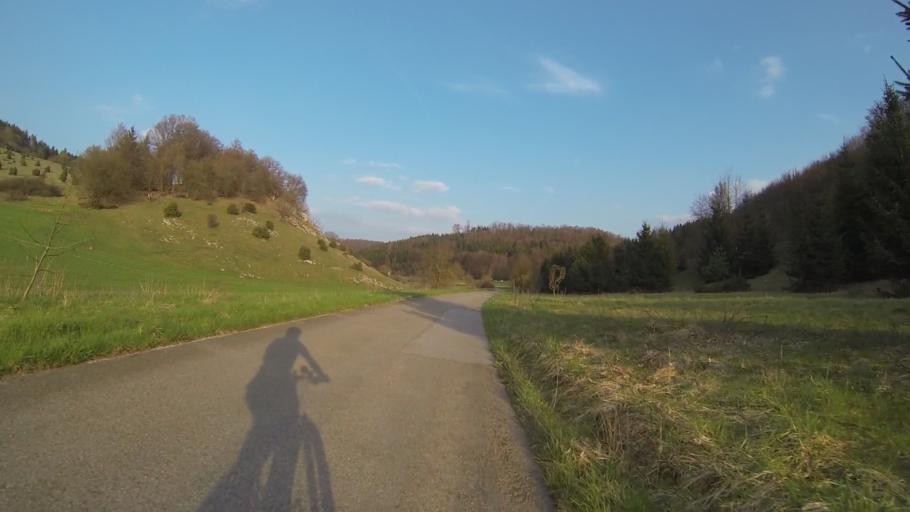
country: DE
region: Baden-Wuerttemberg
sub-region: Regierungsbezirk Stuttgart
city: Heidenheim an der Brenz
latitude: 48.6955
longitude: 10.1929
